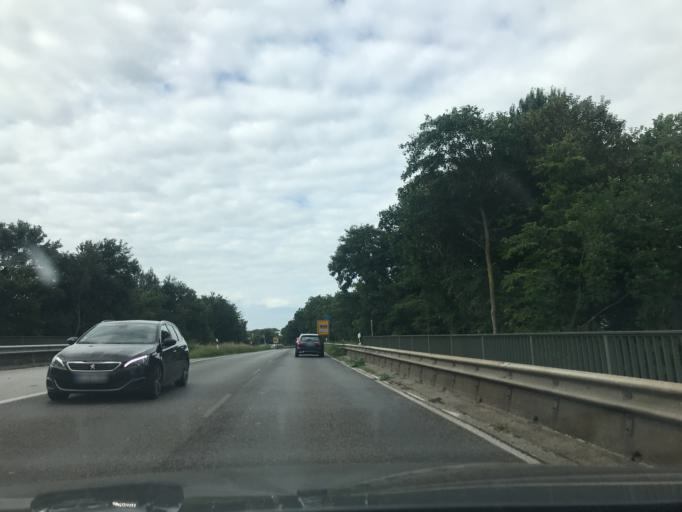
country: DE
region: North Rhine-Westphalia
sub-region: Regierungsbezirk Dusseldorf
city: Neuss
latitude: 51.1651
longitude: 6.7237
